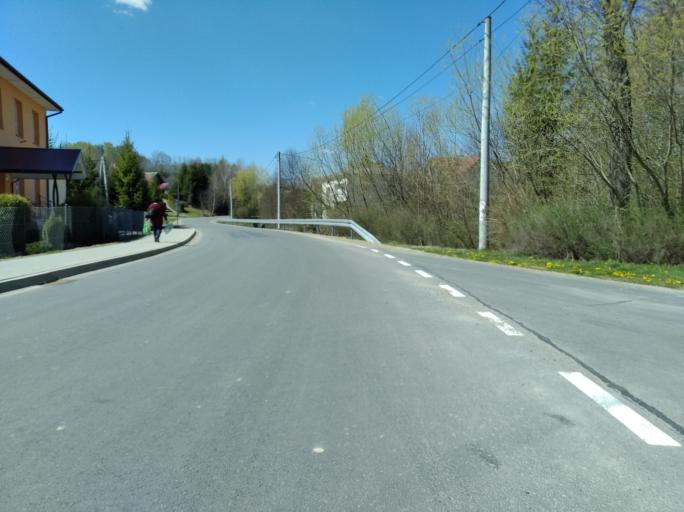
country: PL
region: Subcarpathian Voivodeship
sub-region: Powiat brzozowski
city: Jablonka
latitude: 49.7167
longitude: 22.1309
